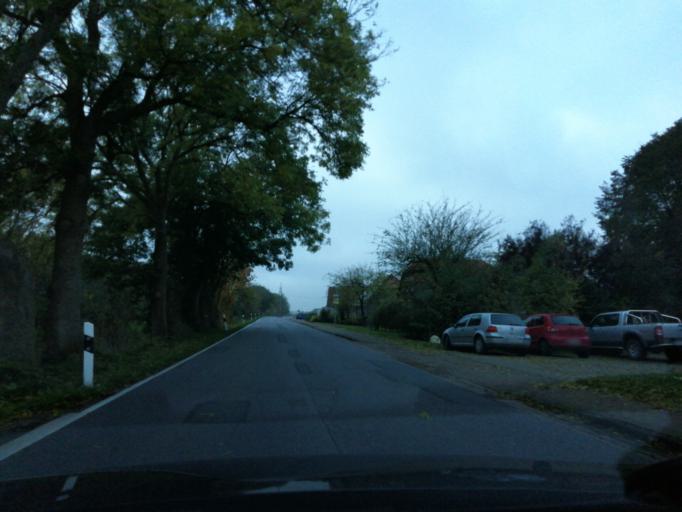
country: DE
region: Lower Saxony
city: Jever
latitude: 53.6730
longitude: 7.8643
